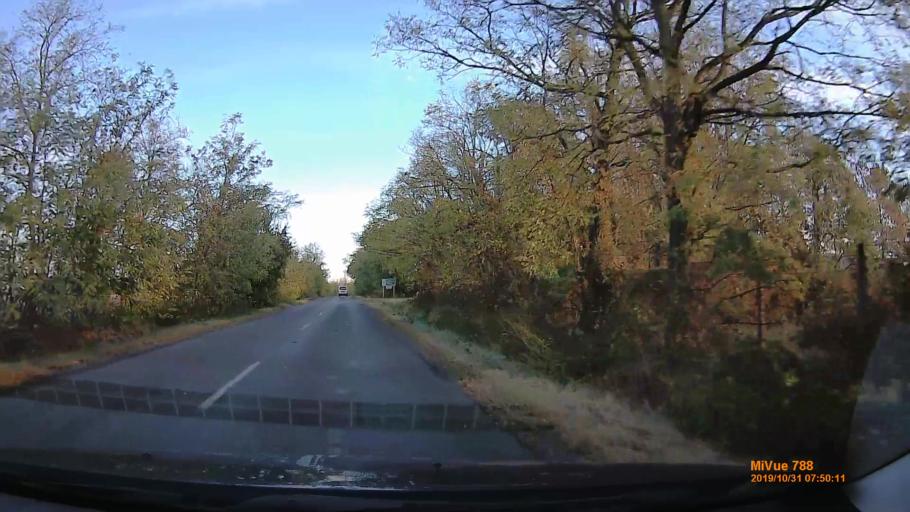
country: HU
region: Pest
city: Pilis
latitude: 47.3010
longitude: 19.5616
